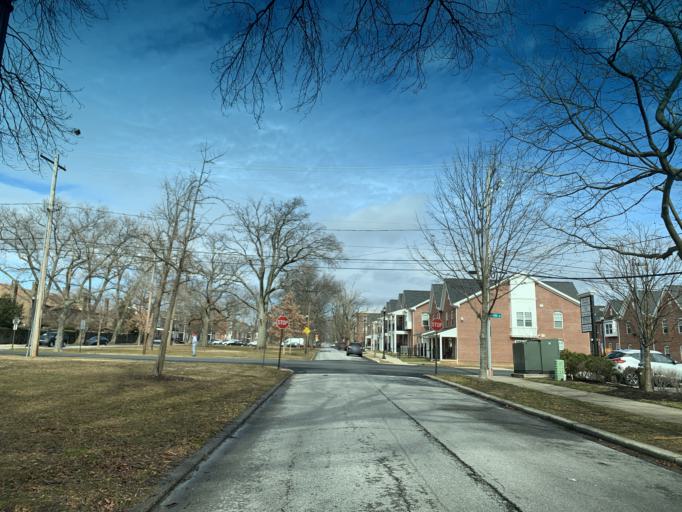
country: US
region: Delaware
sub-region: New Castle County
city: Elsmere
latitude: 39.7492
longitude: -75.5739
